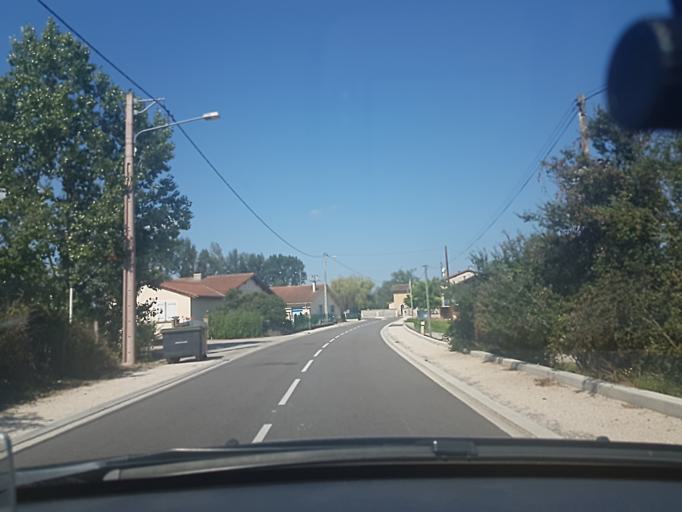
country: FR
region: Midi-Pyrenees
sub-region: Departement de l'Ariege
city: Mirepoix
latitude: 43.0790
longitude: 1.7755
